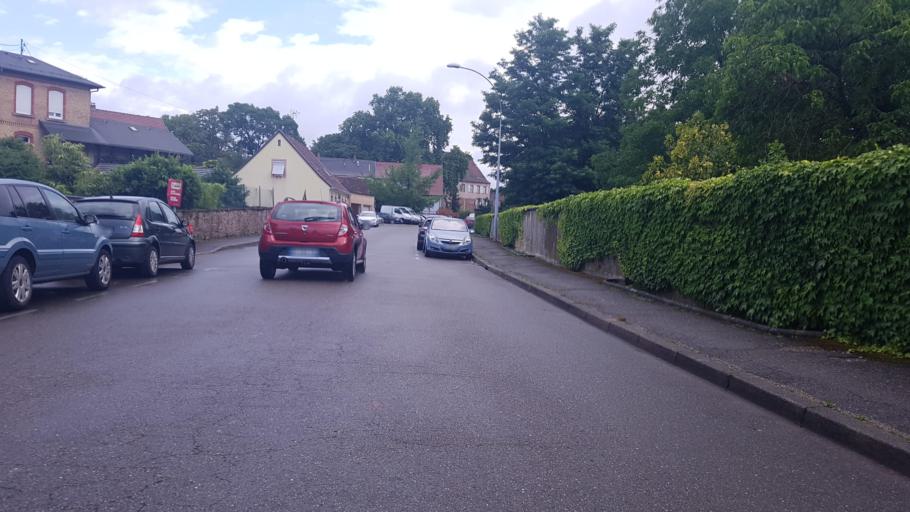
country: FR
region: Alsace
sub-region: Departement du Bas-Rhin
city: Saverne
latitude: 48.7380
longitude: 7.3637
